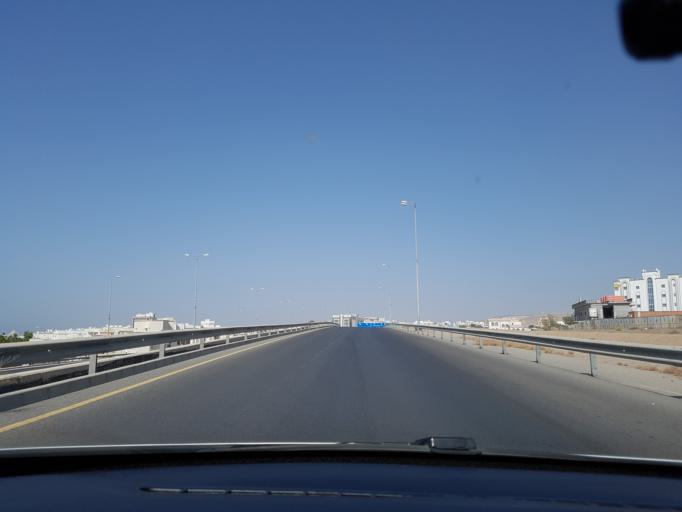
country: OM
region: Muhafazat Masqat
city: Bawshar
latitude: 23.5897
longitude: 58.4400
